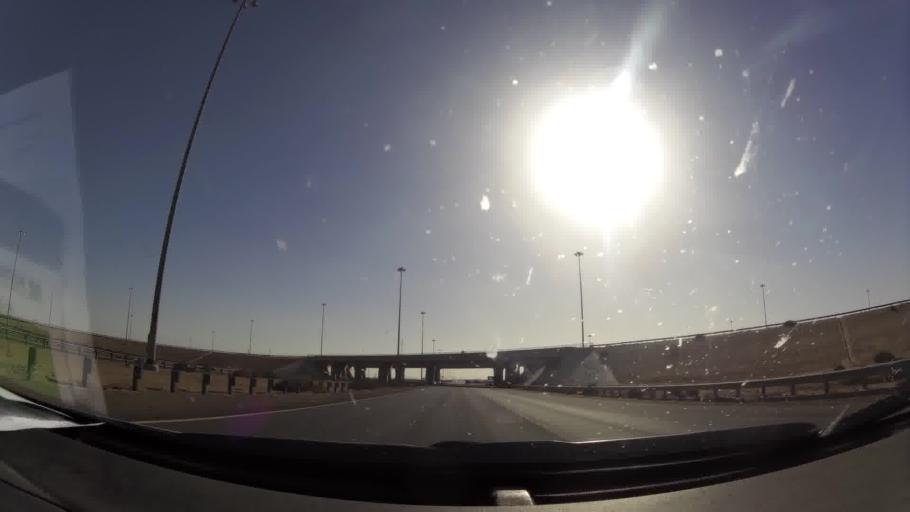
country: KW
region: Al Asimah
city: Kuwait City
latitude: 29.6101
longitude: 47.9148
